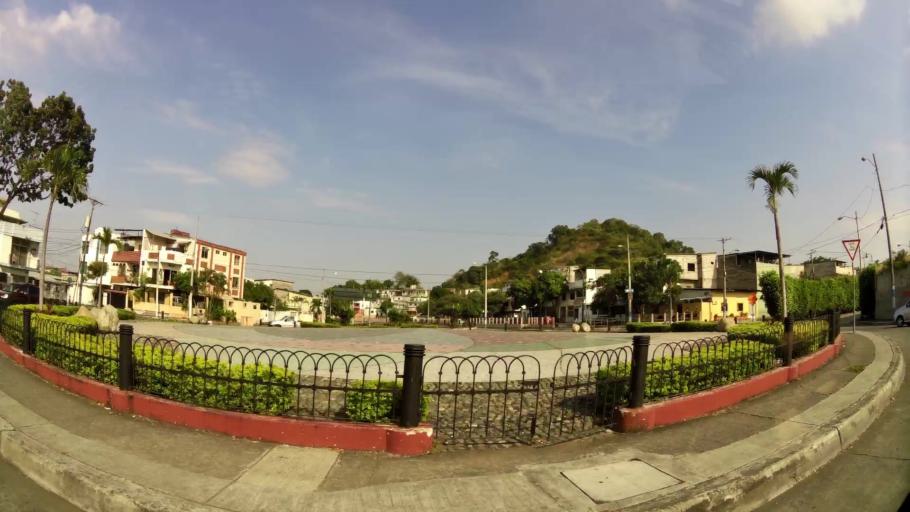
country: EC
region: Guayas
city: Guayaquil
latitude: -2.1860
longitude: -79.9028
